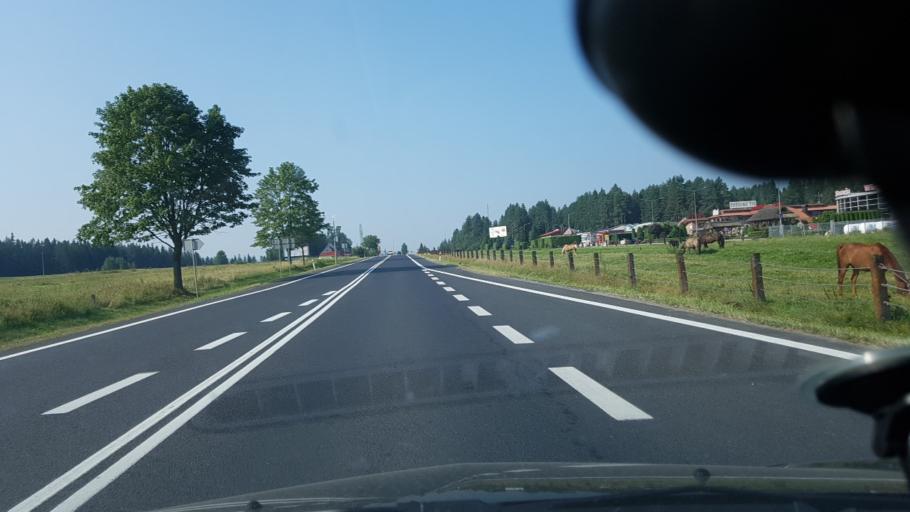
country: PL
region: Lesser Poland Voivodeship
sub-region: Powiat nowotarski
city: Chyzne
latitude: 49.4168
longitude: 19.6666
